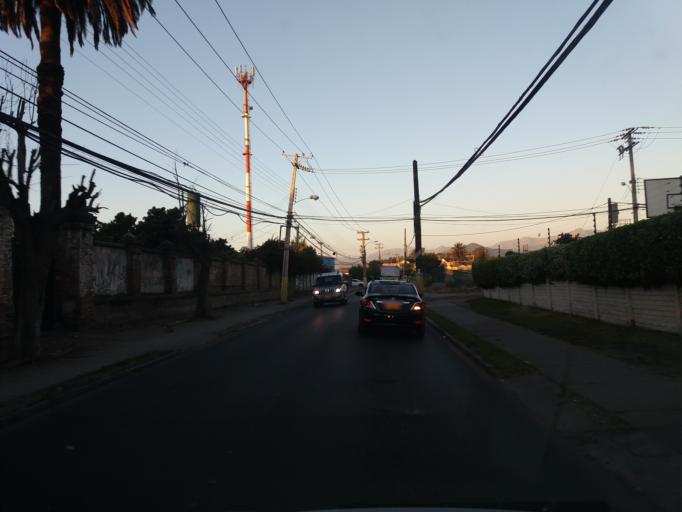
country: CL
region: Valparaiso
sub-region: Provincia de Quillota
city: Quillota
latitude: -32.8884
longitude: -71.2604
